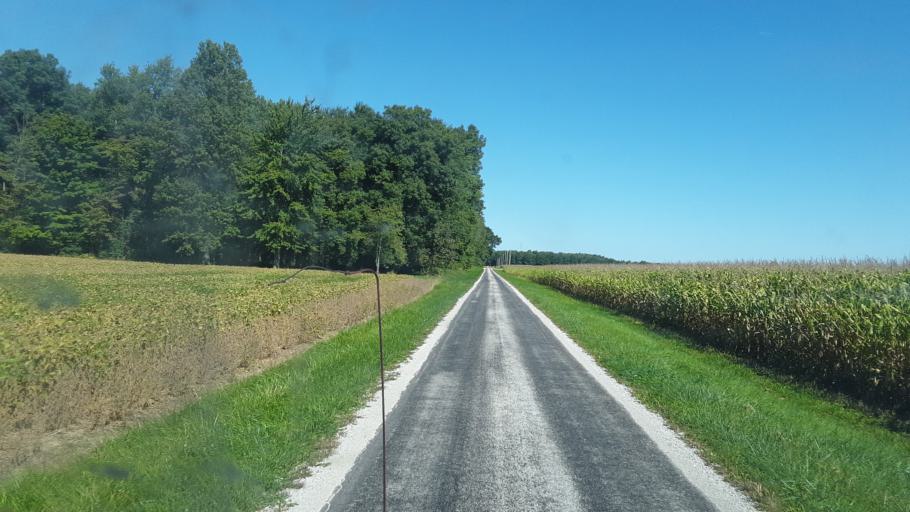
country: US
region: Ohio
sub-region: Crawford County
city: Bucyrus
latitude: 40.9869
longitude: -83.0355
